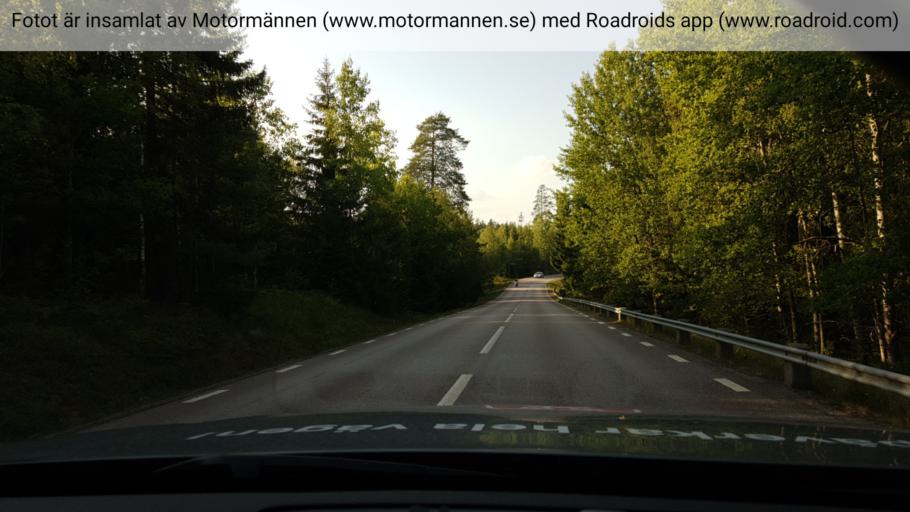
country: SE
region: Soedermanland
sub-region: Strangnas Kommun
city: Mariefred
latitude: 59.1838
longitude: 17.1889
